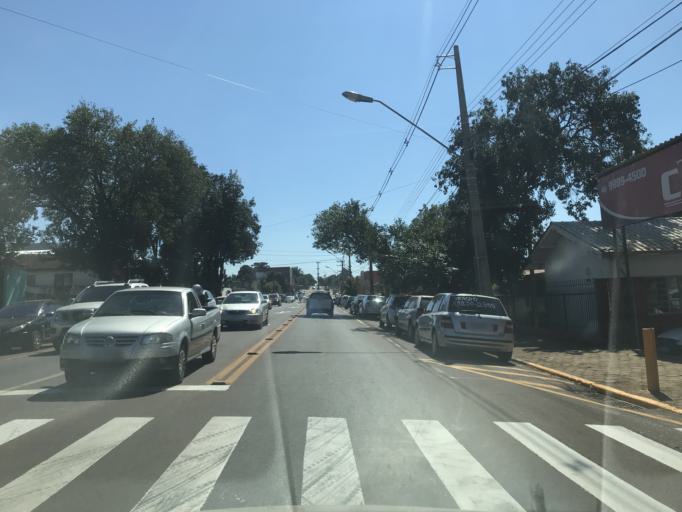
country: BR
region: Parana
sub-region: Toledo
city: Toledo
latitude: -24.7300
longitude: -53.7361
